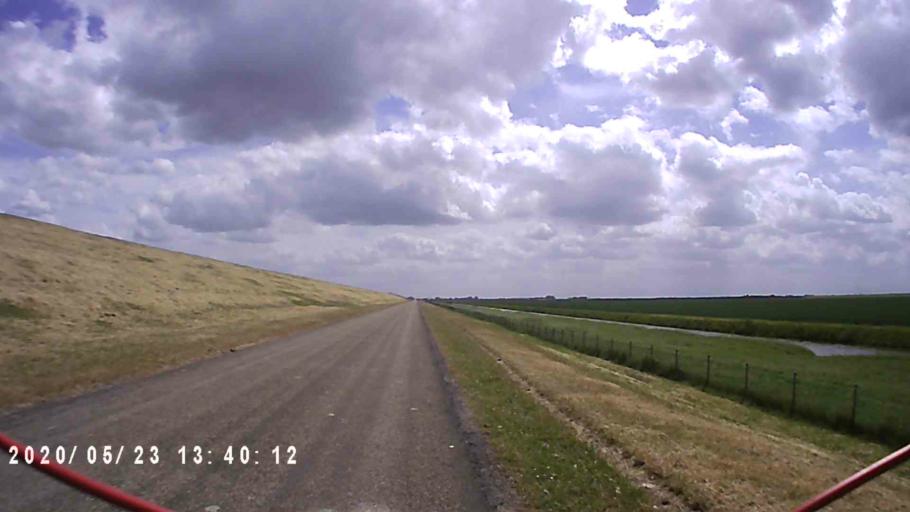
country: NL
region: Groningen
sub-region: Gemeente  Oldambt
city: Winschoten
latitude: 53.2609
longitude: 7.0754
